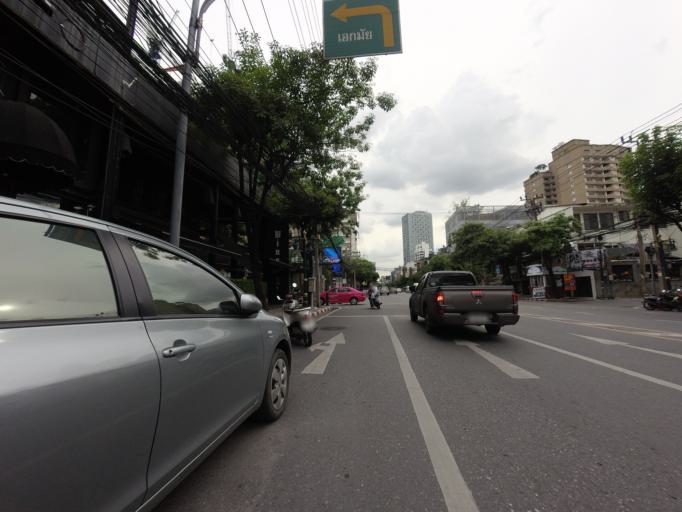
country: TH
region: Bangkok
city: Watthana
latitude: 13.7326
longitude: 100.5822
